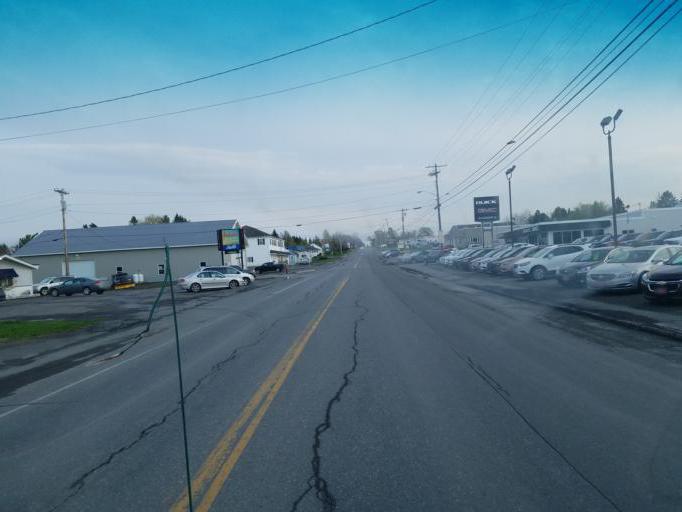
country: US
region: Maine
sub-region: Aroostook County
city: Caribou
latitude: 46.8471
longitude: -68.0108
